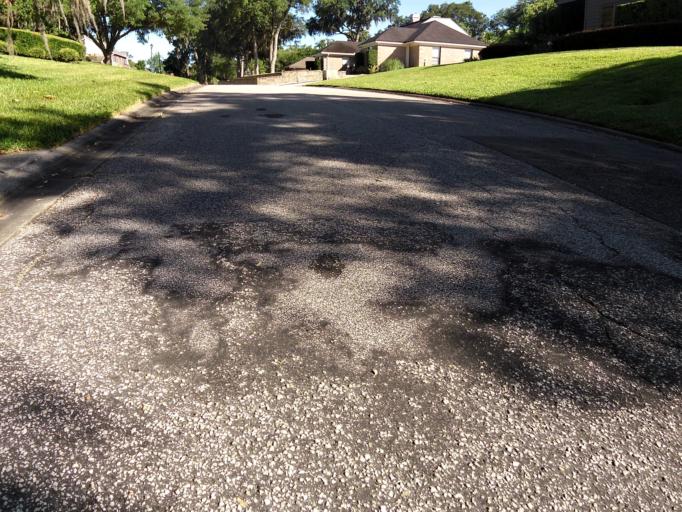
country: US
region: Florida
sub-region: Duval County
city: Jacksonville
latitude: 30.3149
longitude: -81.6190
